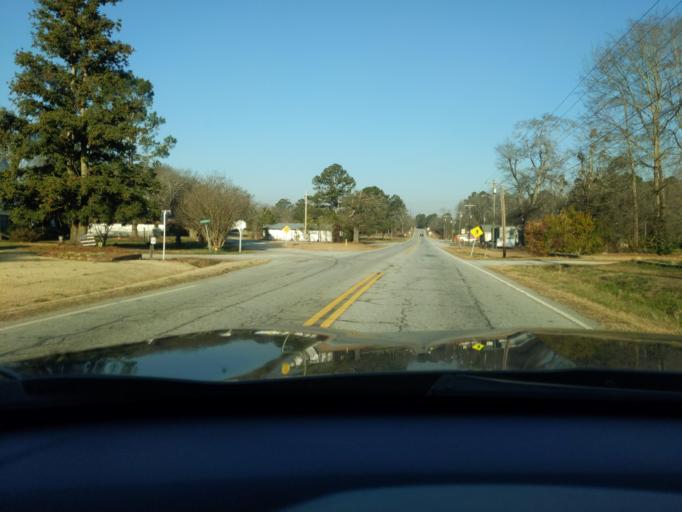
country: US
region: South Carolina
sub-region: Newberry County
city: Newberry
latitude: 34.2177
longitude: -81.7150
